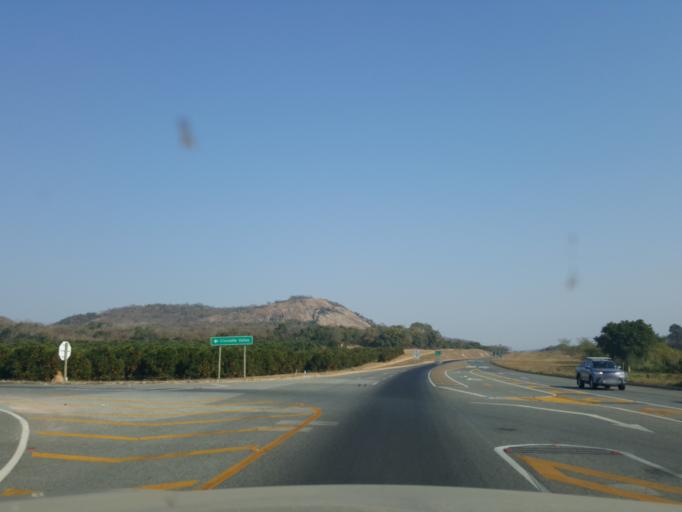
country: ZA
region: Mpumalanga
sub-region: Ehlanzeni District
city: Nelspruit
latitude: -25.4688
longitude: 31.0778
